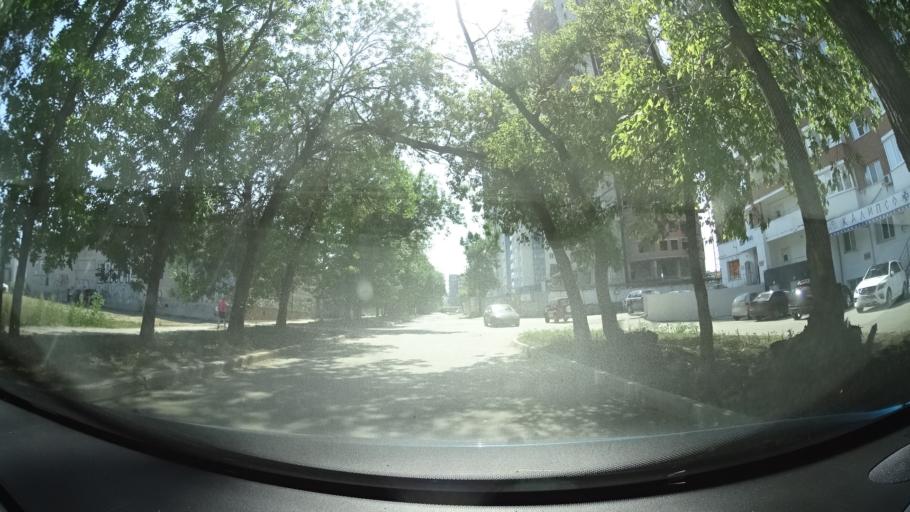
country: RU
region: Samara
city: Samara
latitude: 53.2147
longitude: 50.1468
